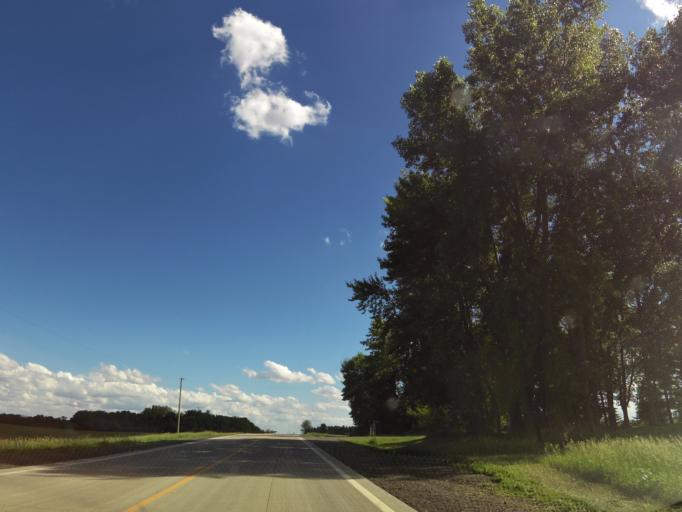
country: US
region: Minnesota
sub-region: Wright County
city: Cokato
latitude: 44.9742
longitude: -94.1753
